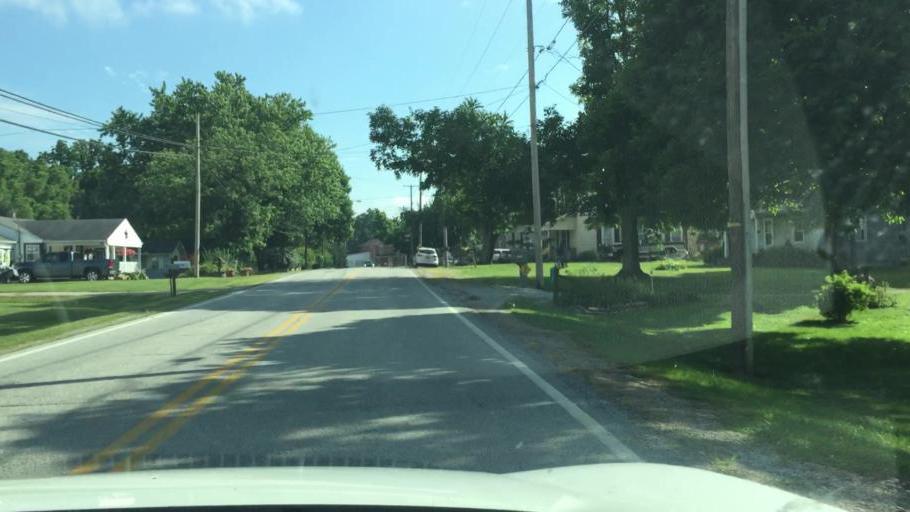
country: US
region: Ohio
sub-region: Clark County
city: Northridge
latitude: 39.9943
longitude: -83.7148
